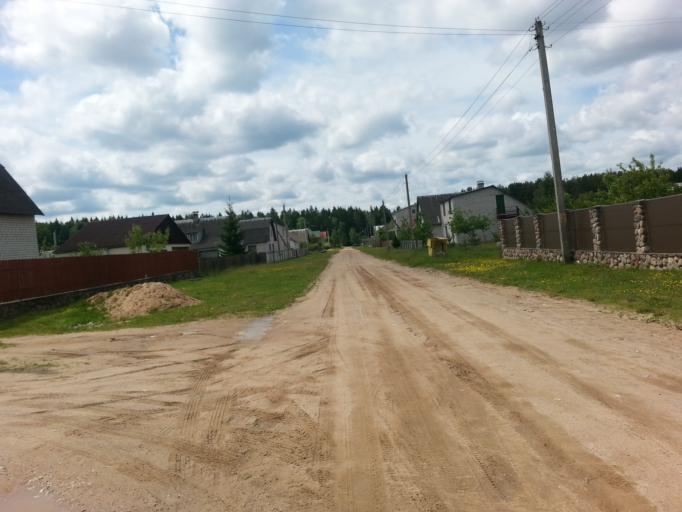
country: BY
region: Minsk
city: Narach
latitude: 54.9245
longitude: 26.6881
